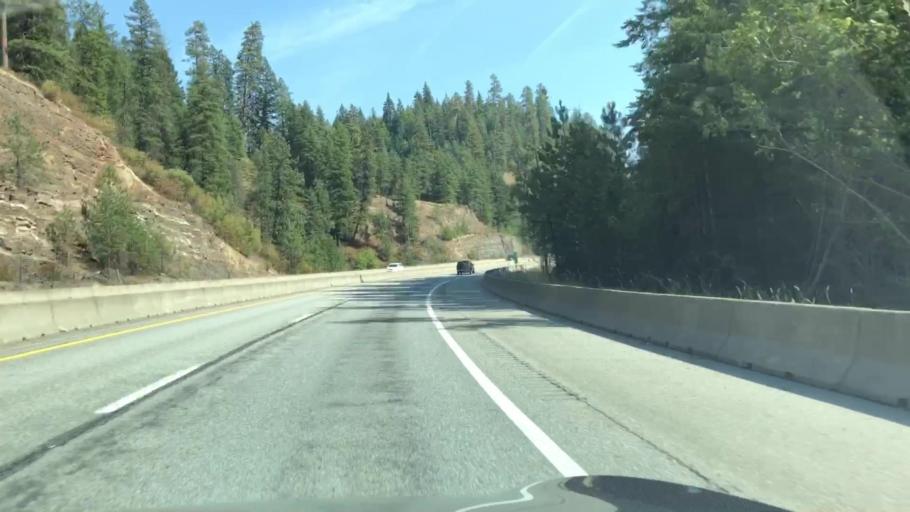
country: US
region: Idaho
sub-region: Kootenai County
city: Coeur d'Alene
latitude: 47.6266
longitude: -116.5897
